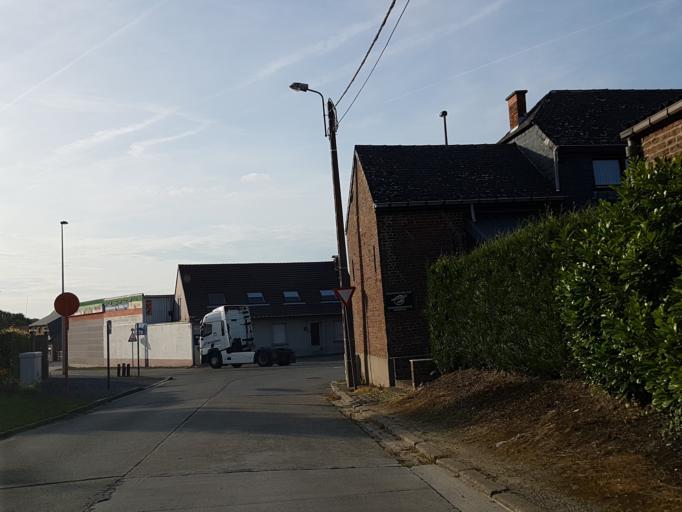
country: BE
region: Flanders
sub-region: Provincie Vlaams-Brabant
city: Opwijk
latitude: 50.9508
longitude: 4.1364
